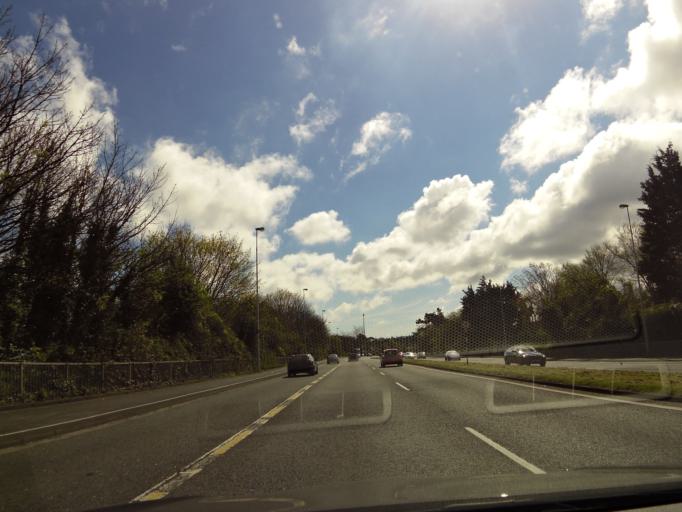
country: IE
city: Booterstown
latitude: 53.2915
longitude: -6.1982
